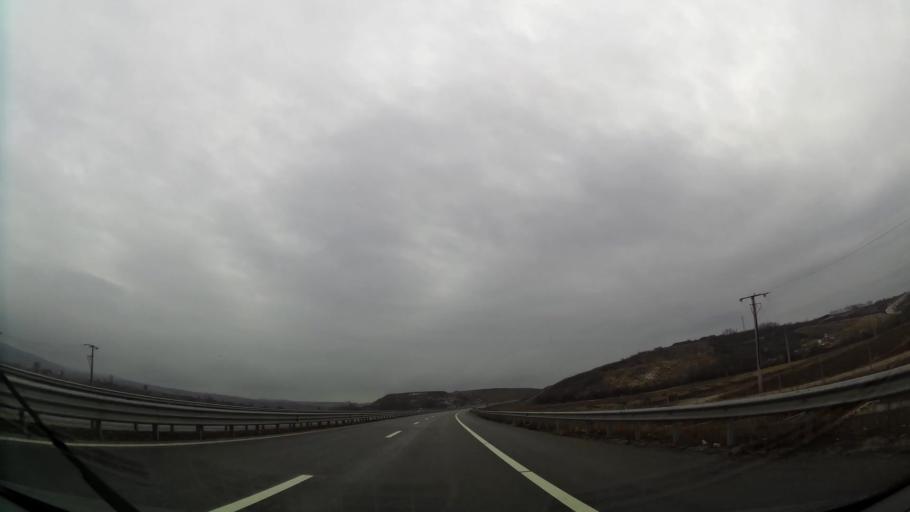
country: XK
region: Ferizaj
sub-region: Komuna e Ferizajt
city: Ferizaj
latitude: 42.4419
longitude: 21.1982
